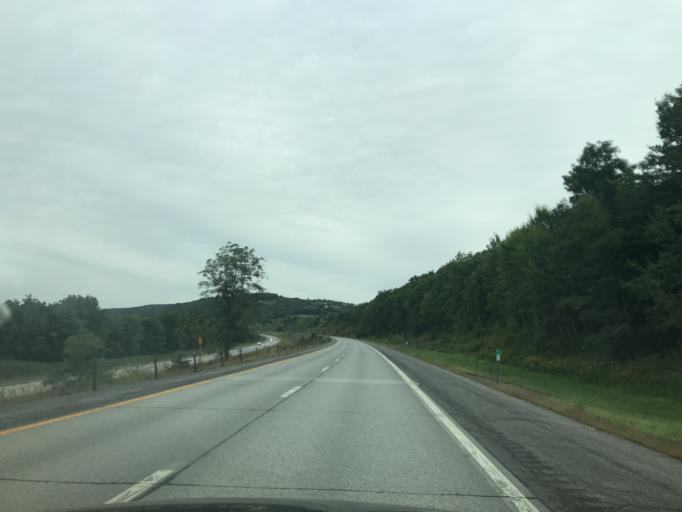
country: US
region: New York
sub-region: Schoharie County
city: Schoharie
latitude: 42.6796
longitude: -74.3838
